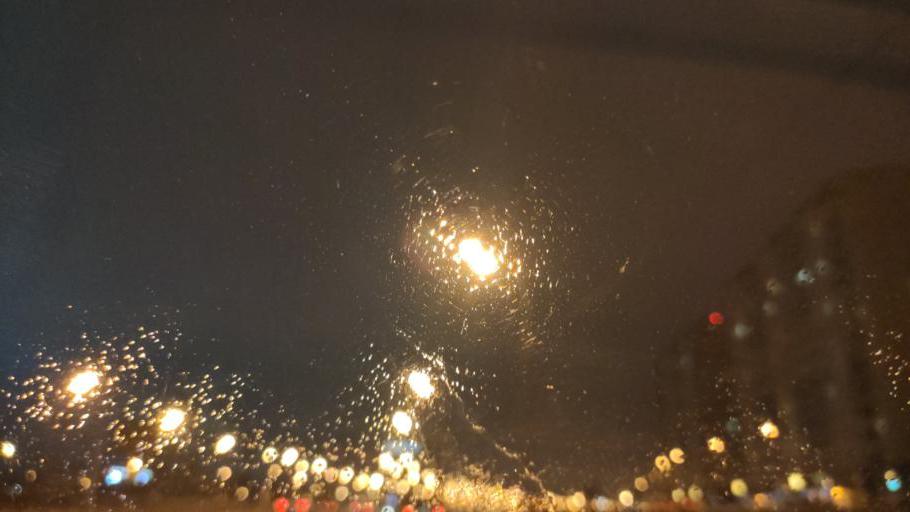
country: RU
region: Moskovskaya
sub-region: Leninskiy Rayon
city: Vnukovo
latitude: 55.6182
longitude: 37.2669
